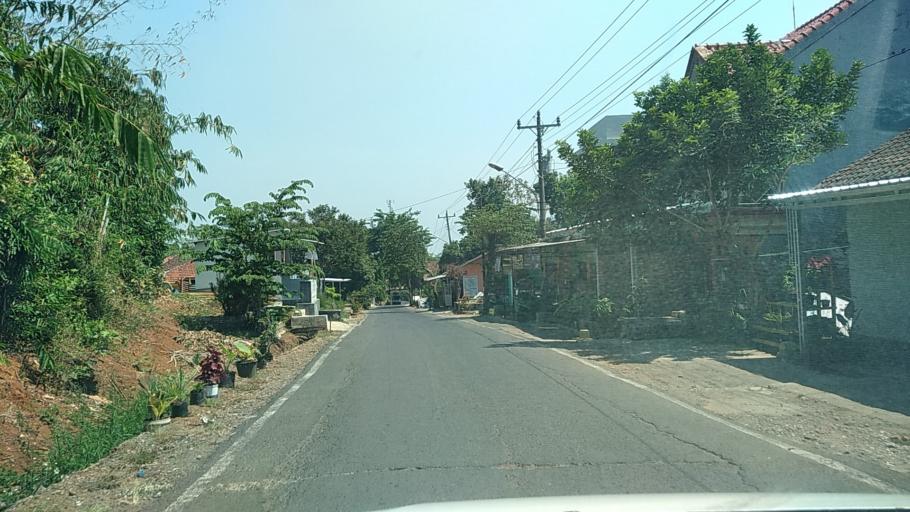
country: ID
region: Central Java
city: Ungaran
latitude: -7.0931
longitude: 110.3605
